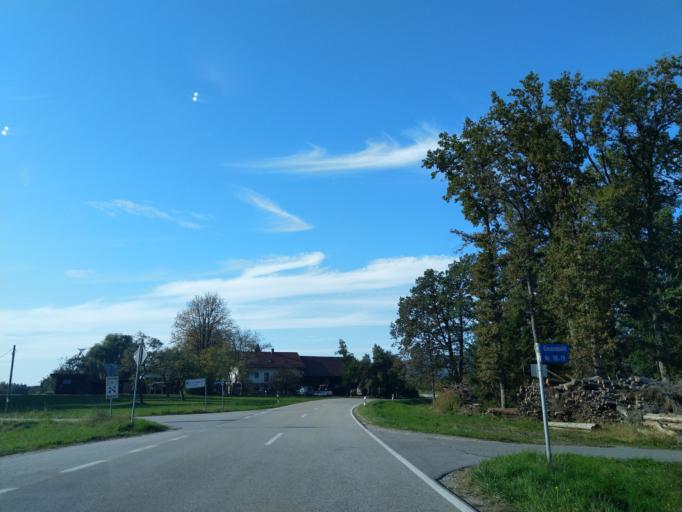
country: DE
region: Bavaria
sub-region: Lower Bavaria
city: Bernried
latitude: 48.8910
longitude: 12.9084
